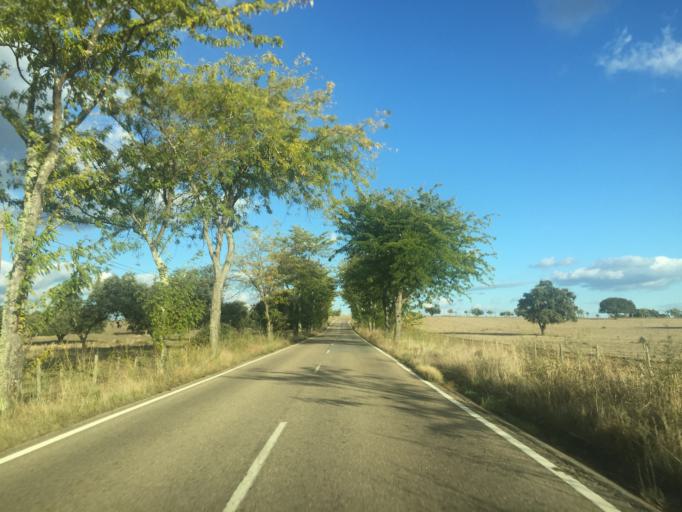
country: PT
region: Portalegre
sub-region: Alter do Chao
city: Alter do Chao
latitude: 39.2039
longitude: -7.7444
